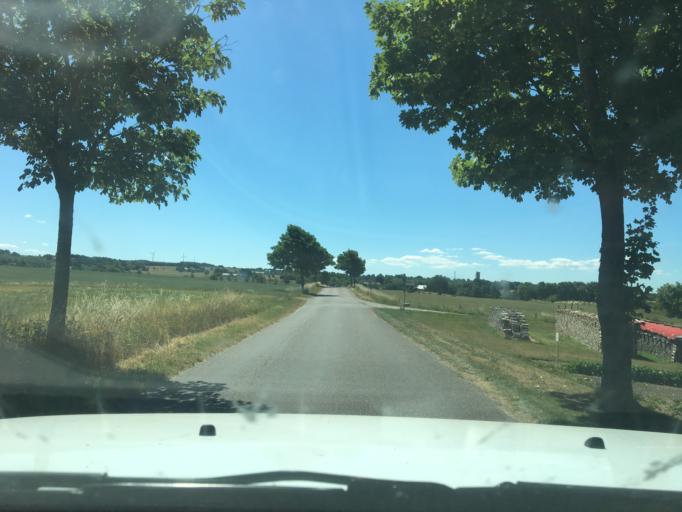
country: DK
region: Central Jutland
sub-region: Syddjurs Kommune
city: Hornslet
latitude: 56.3504
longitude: 10.3892
